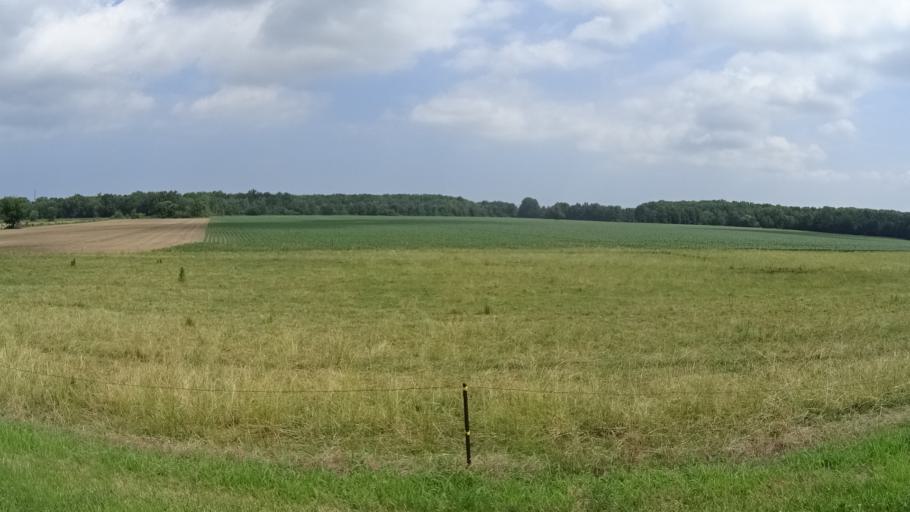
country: US
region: Ohio
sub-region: Lorain County
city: Vermilion
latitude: 41.3784
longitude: -82.3594
